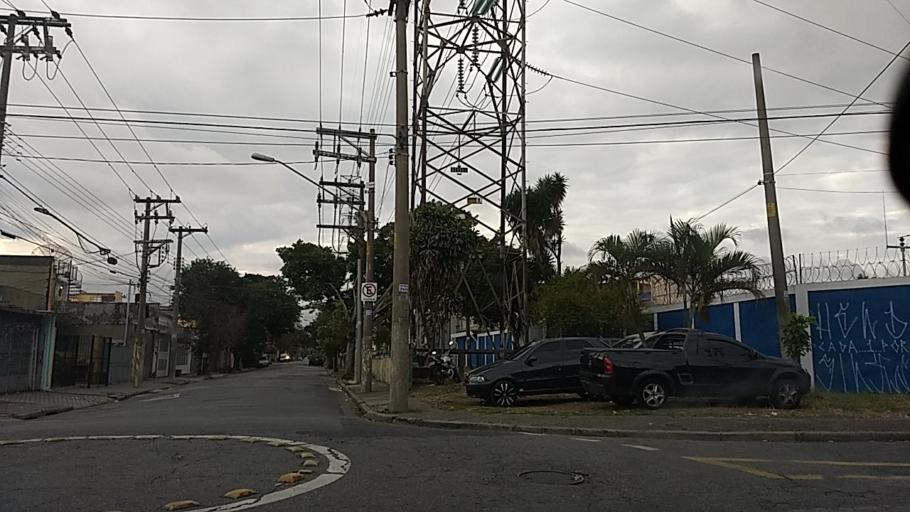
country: BR
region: Sao Paulo
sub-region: Sao Paulo
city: Sao Paulo
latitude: -23.5182
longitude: -46.5988
